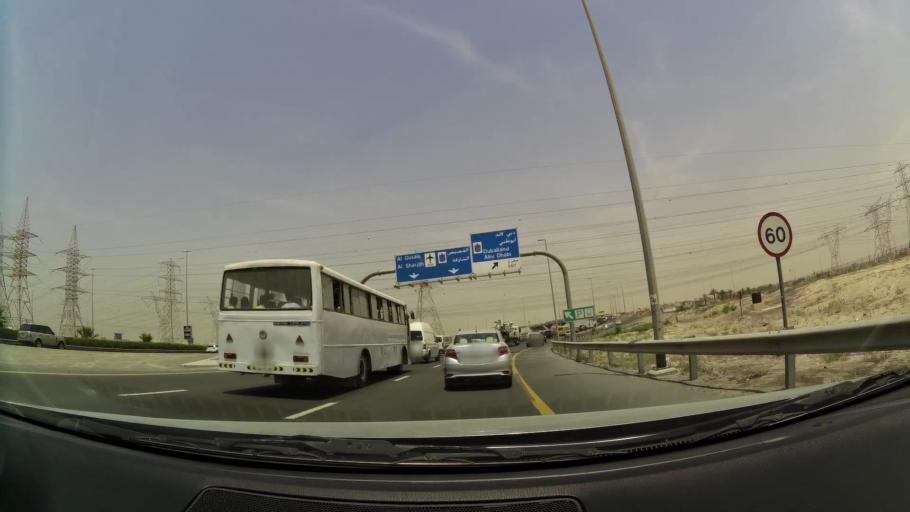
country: AE
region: Ash Shariqah
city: Sharjah
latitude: 25.2119
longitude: 55.3980
